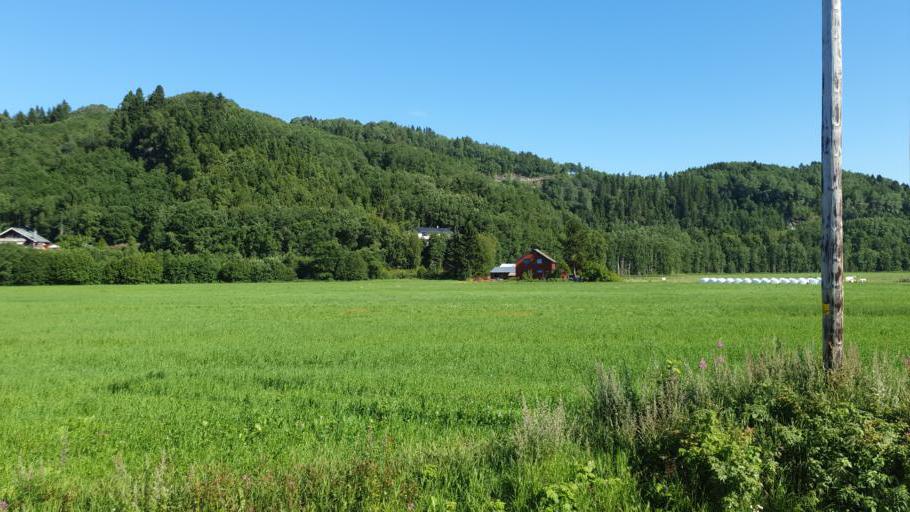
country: NO
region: Sor-Trondelag
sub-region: Orkdal
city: Orkanger
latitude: 63.2085
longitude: 9.7866
